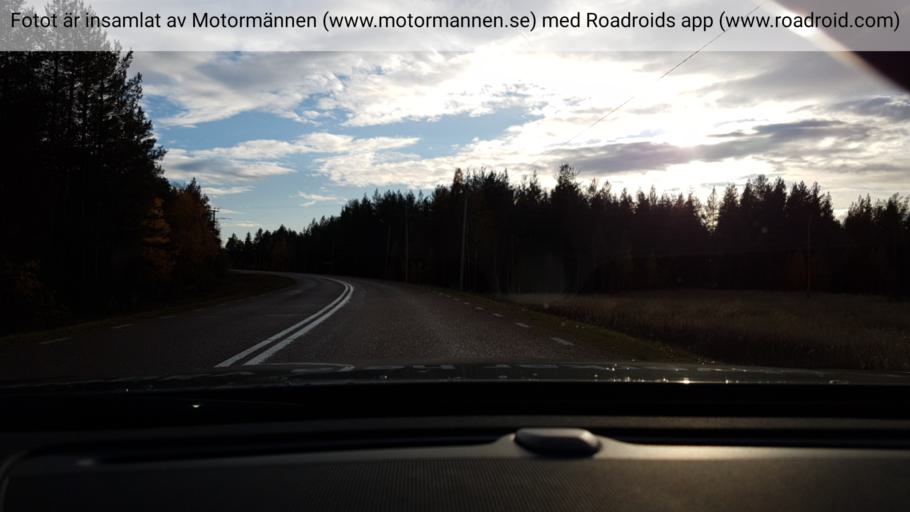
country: SE
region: Norrbotten
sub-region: Pajala Kommun
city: Pajala
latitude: 67.1647
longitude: 22.6362
